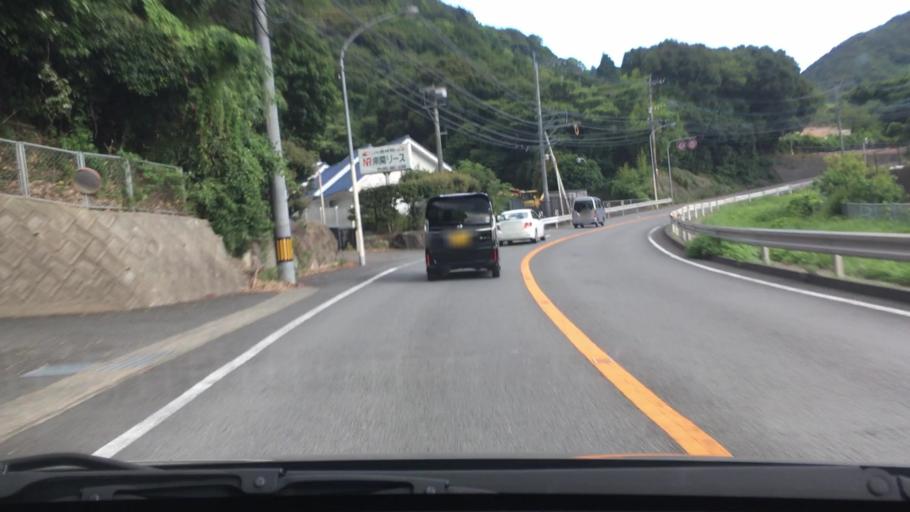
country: JP
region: Nagasaki
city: Togitsu
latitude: 32.8145
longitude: 129.8089
